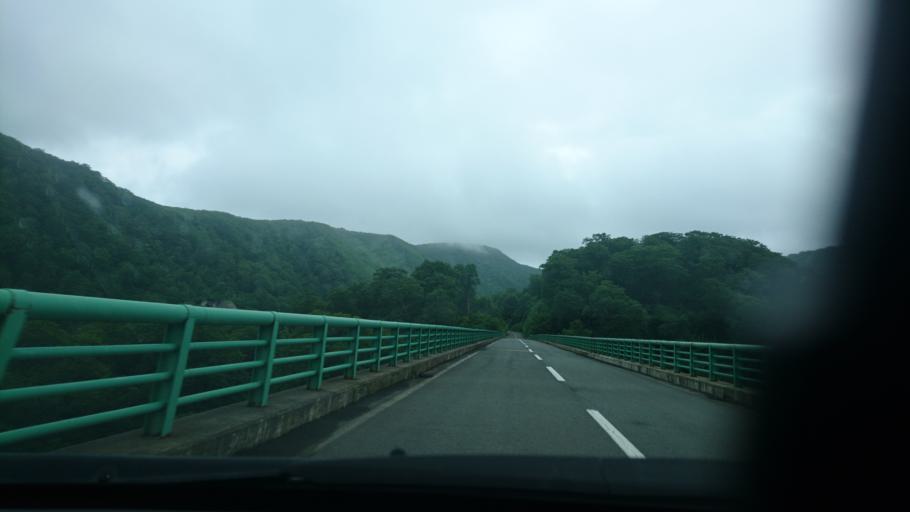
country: JP
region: Akita
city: Yuzawa
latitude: 39.1462
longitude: 140.7677
